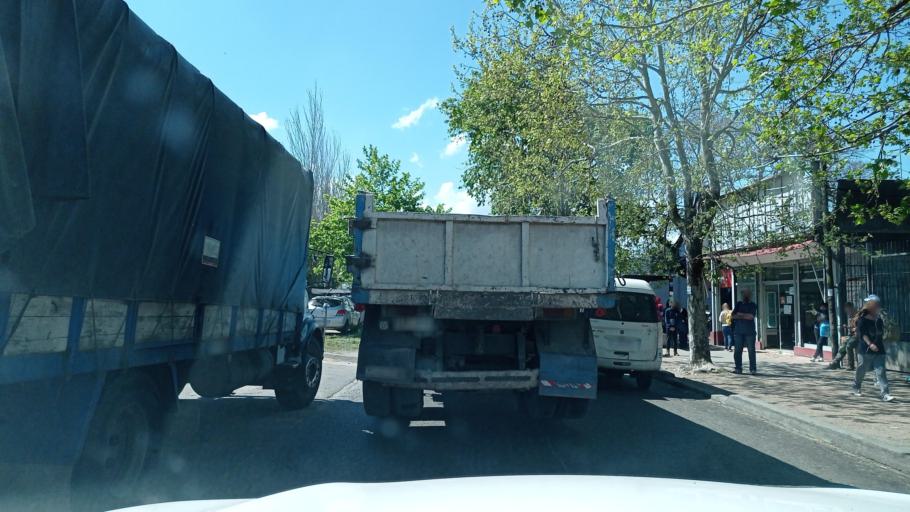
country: UY
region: Montevideo
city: Montevideo
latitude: -34.8277
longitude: -56.1408
